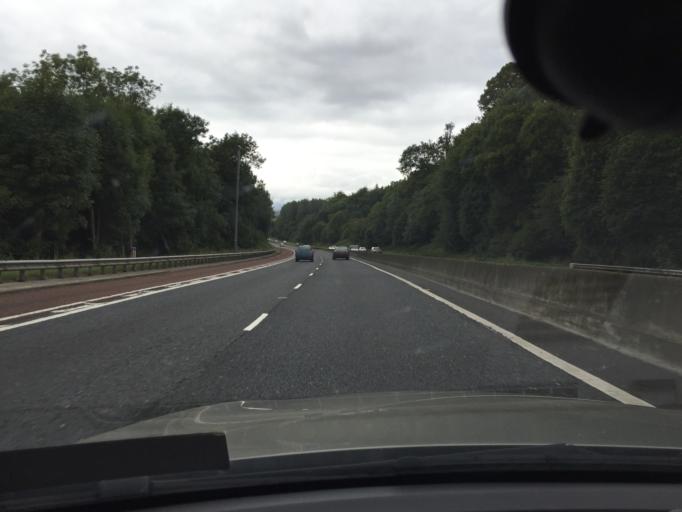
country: GB
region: Northern Ireland
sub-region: Lisburn District
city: Lisburn
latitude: 54.5431
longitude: -5.9938
